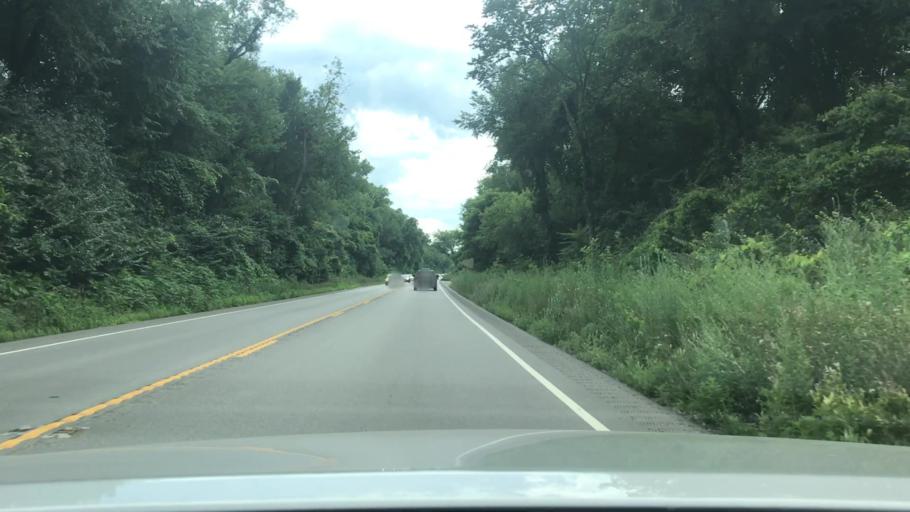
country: US
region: Illinois
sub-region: DuPage County
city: Burr Ridge
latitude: 41.7102
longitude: -87.9164
